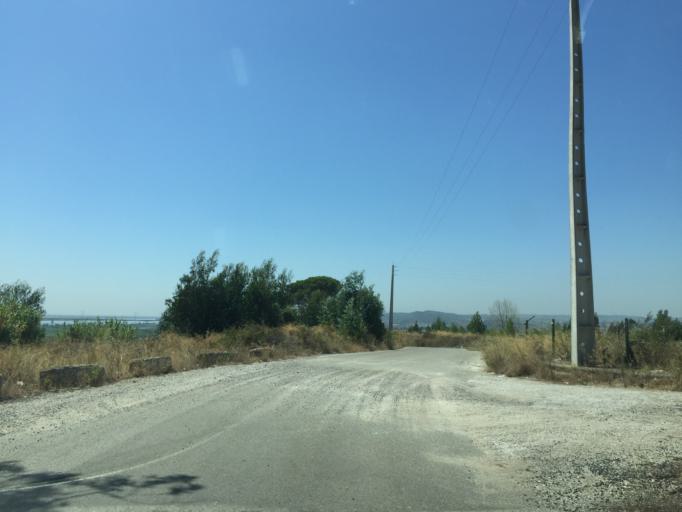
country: PT
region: Lisbon
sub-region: Alenquer
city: Carregado
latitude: 39.0471
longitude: -8.9278
